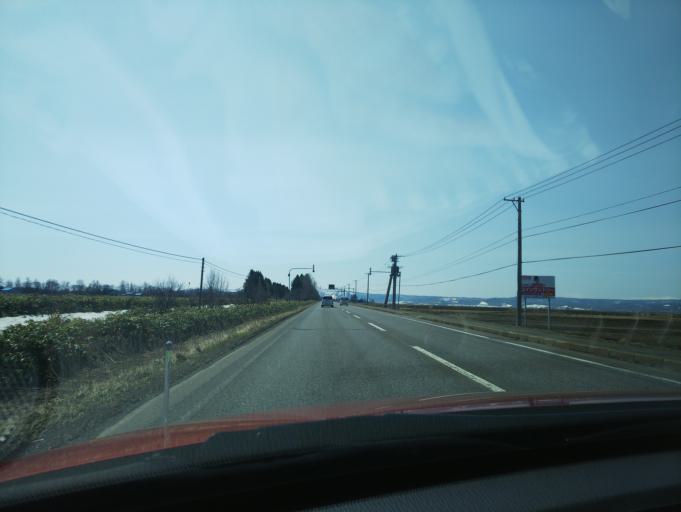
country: JP
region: Hokkaido
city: Nayoro
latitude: 44.3100
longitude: 142.4468
